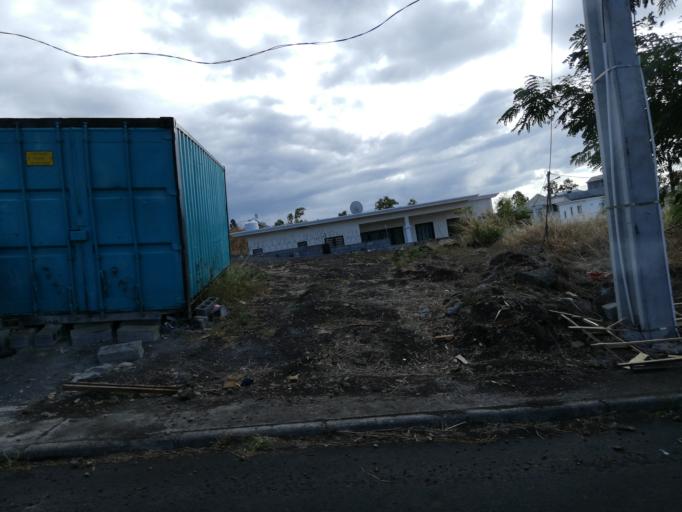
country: MU
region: Black River
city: Petite Riviere
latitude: -20.2029
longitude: 57.4616
